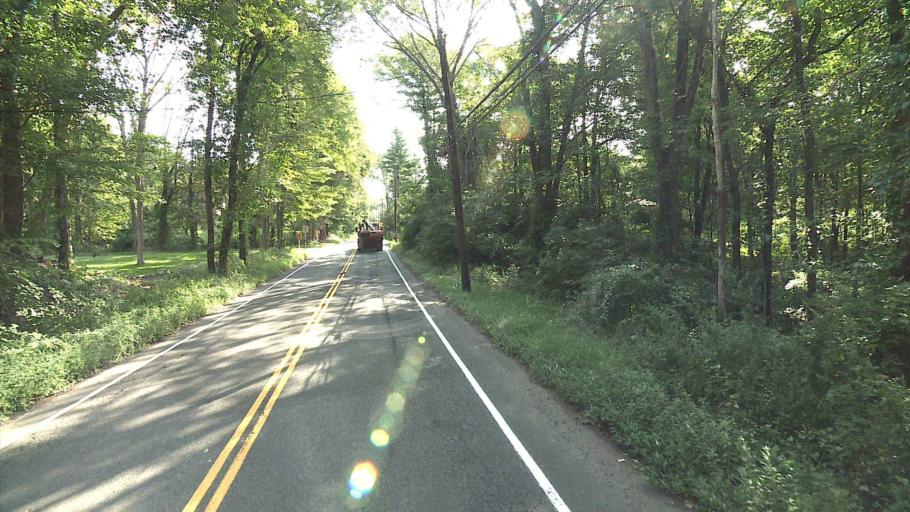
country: US
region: Connecticut
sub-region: Fairfield County
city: Bethel
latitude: 41.3226
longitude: -73.3602
